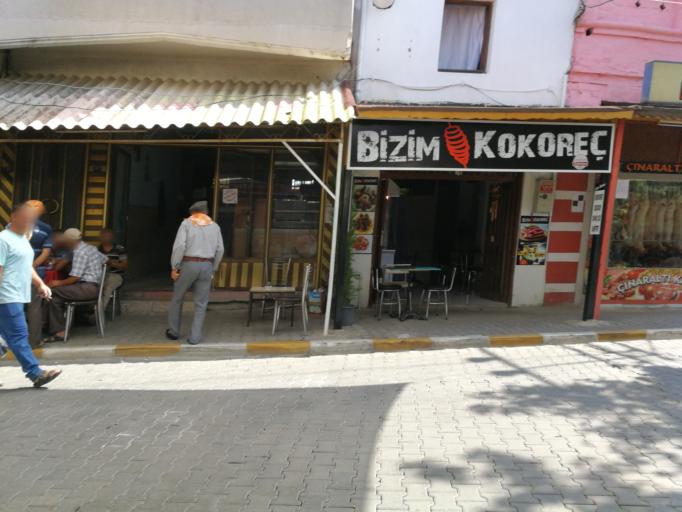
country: TR
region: Izmir
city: Urla
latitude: 38.3220
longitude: 26.7679
